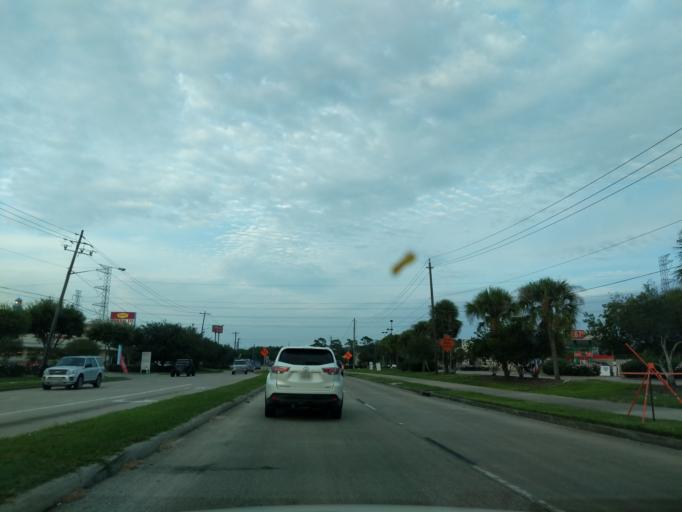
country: US
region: Texas
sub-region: Galveston County
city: Kemah
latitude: 29.5364
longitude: -95.0204
